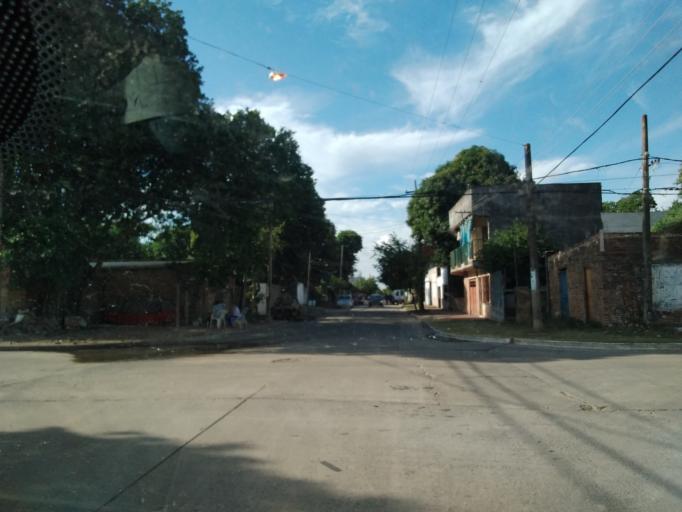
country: AR
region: Corrientes
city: Corrientes
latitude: -27.4660
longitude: -58.8142
